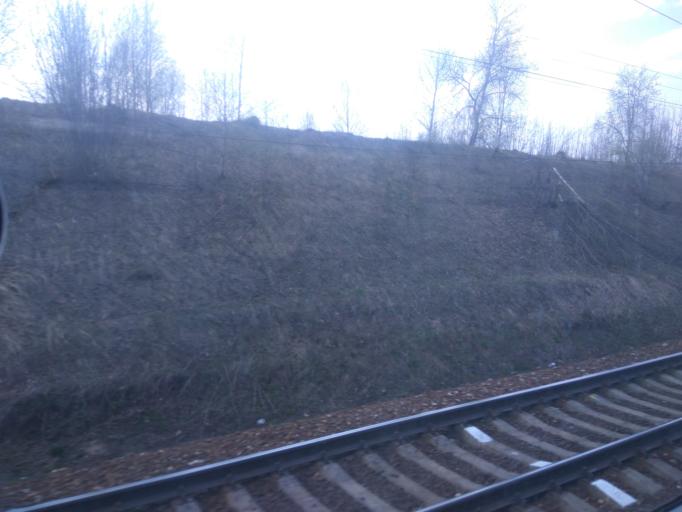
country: RU
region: Moskovskaya
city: Dedenevo
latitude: 56.2648
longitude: 37.5115
